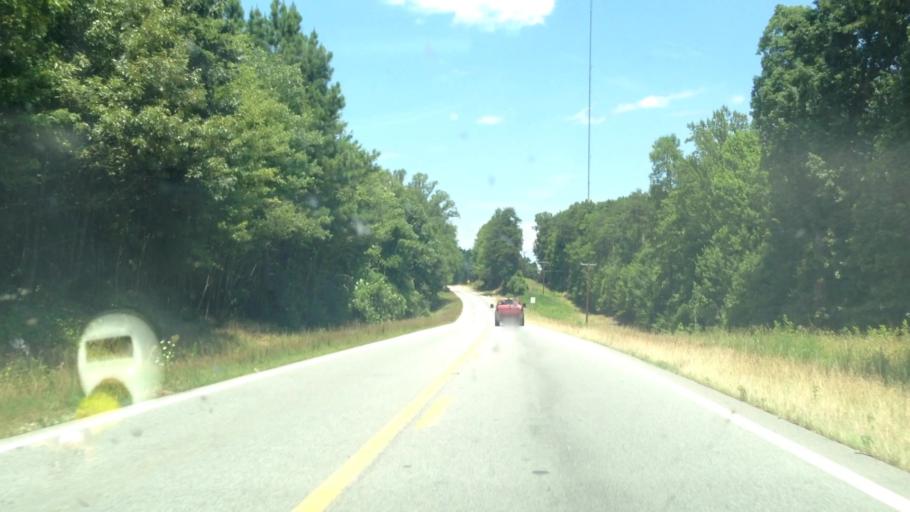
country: US
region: North Carolina
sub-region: Guilford County
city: Stokesdale
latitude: 36.2697
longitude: -79.9475
